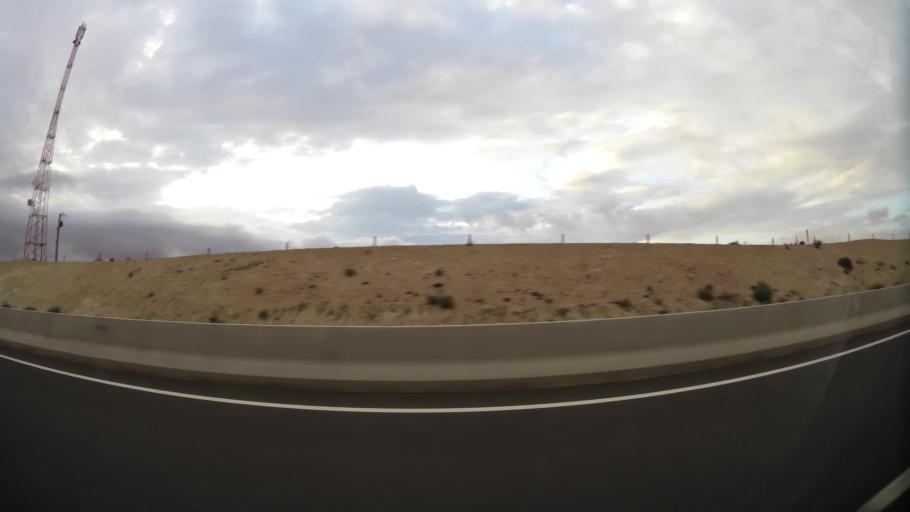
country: MA
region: Taza-Al Hoceima-Taounate
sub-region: Taza
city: Guercif
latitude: 34.4045
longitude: -3.1774
